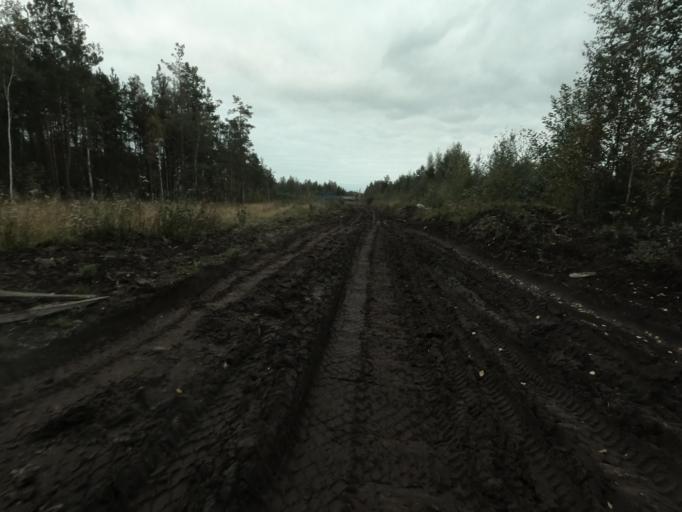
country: RU
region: St.-Petersburg
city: Sapernyy
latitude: 59.7636
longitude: 30.7234
